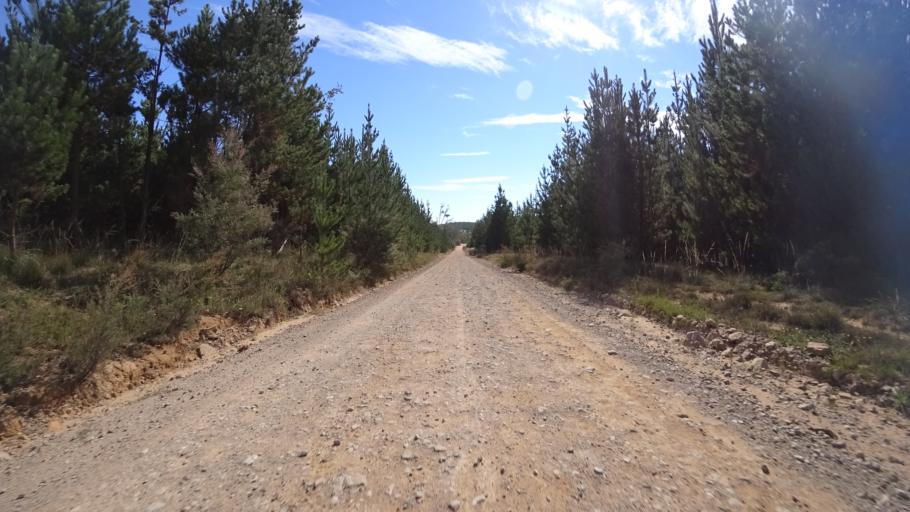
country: AU
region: New South Wales
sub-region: Lithgow
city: Lithgow
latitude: -33.3598
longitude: 150.2500
